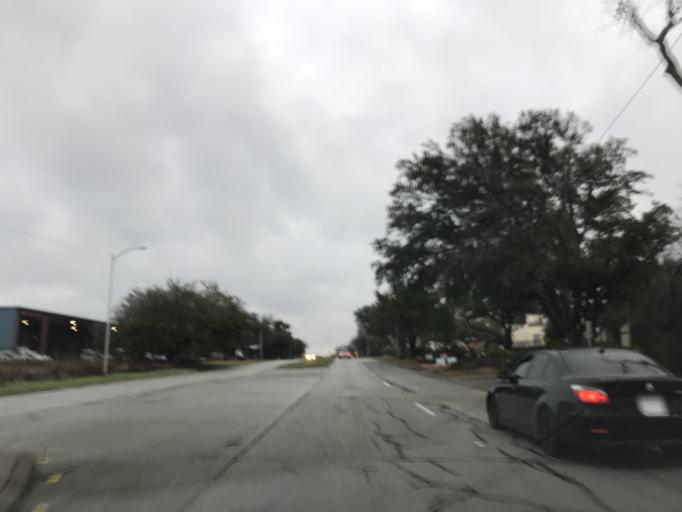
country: US
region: Texas
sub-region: Dallas County
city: Grand Prairie
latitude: 32.7715
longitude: -97.0516
